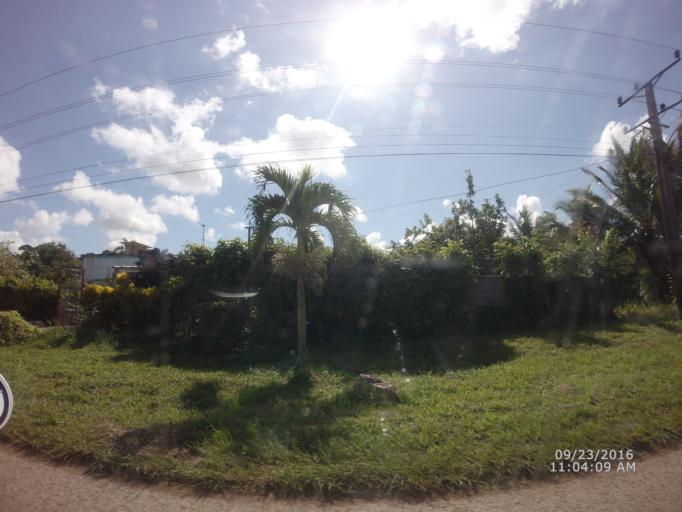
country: CU
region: Mayabeque
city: Jamaica
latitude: 22.9997
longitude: -82.2185
